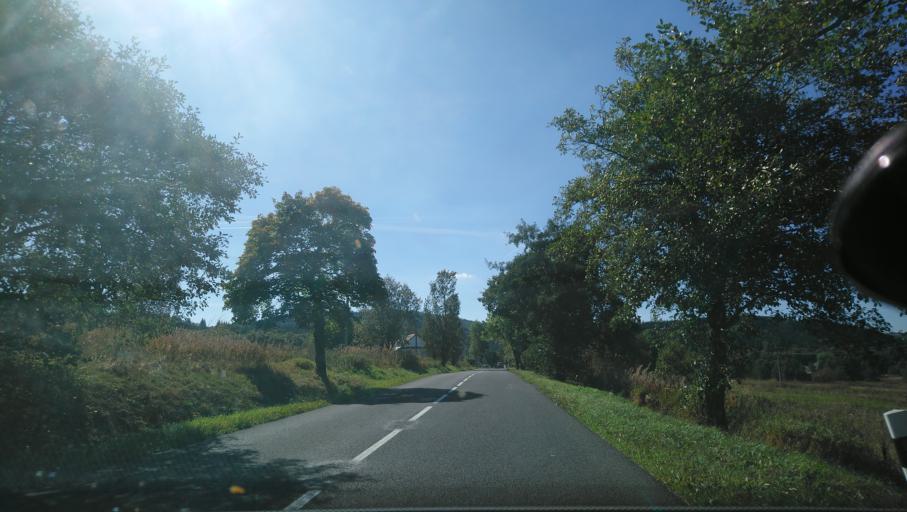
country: CZ
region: Ustecky
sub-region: Okres Chomutov
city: Kovarska
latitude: 50.4432
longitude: 13.0183
